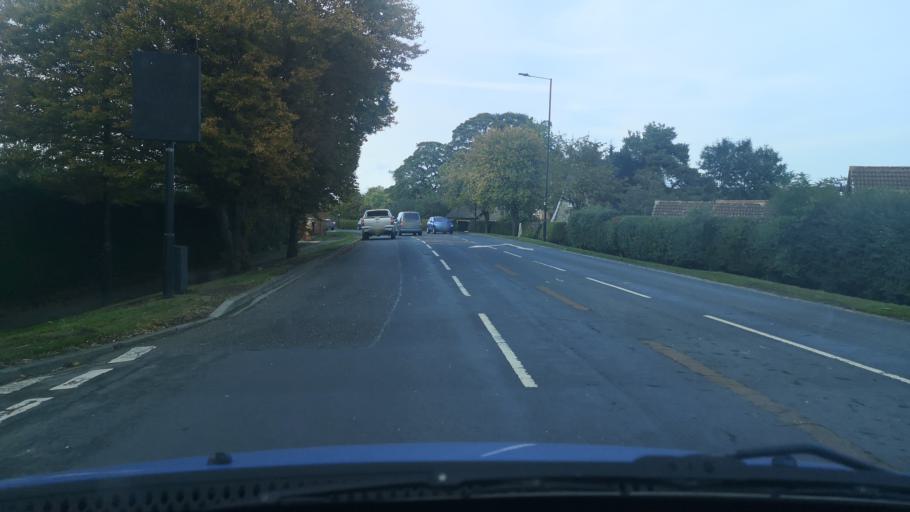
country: GB
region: England
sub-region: Doncaster
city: Hatfield
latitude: 53.6042
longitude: -0.9644
